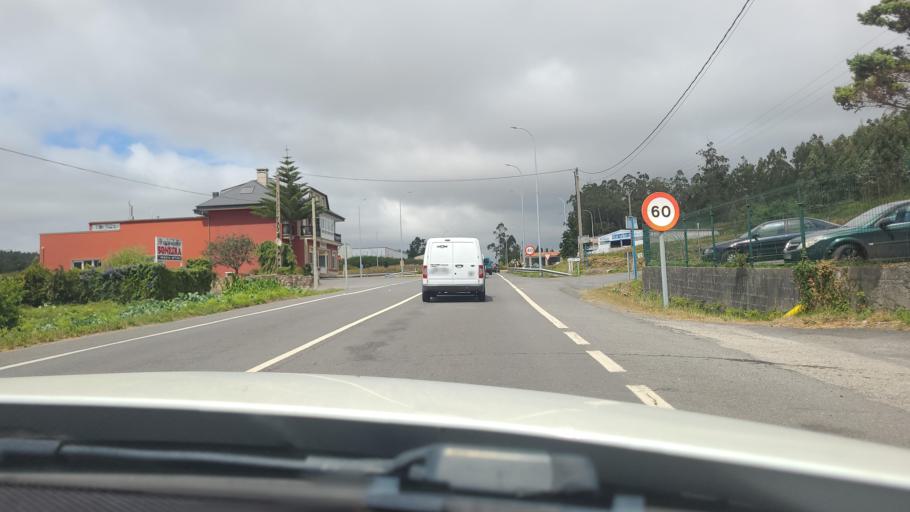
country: ES
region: Galicia
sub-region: Provincia da Coruna
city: Cee
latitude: 42.9762
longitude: -9.1891
